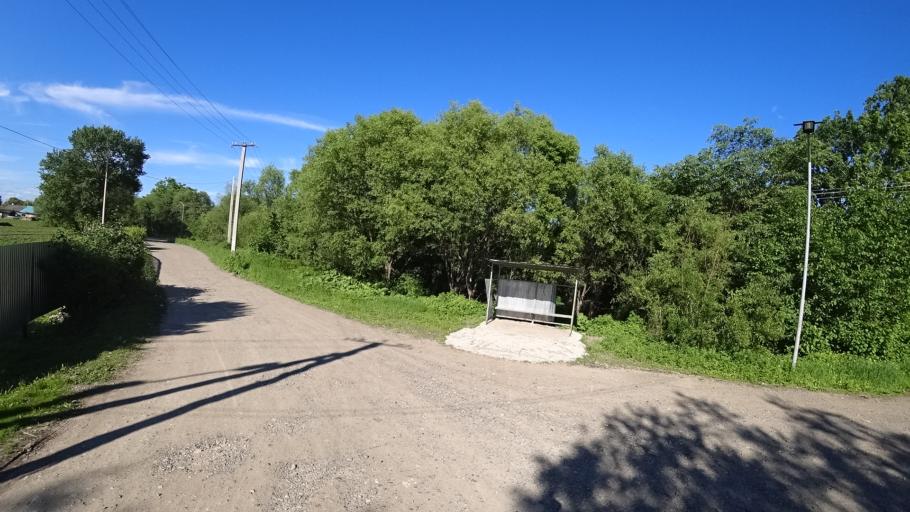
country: RU
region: Khabarovsk Krai
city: Khor
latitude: 47.8871
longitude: 134.9936
